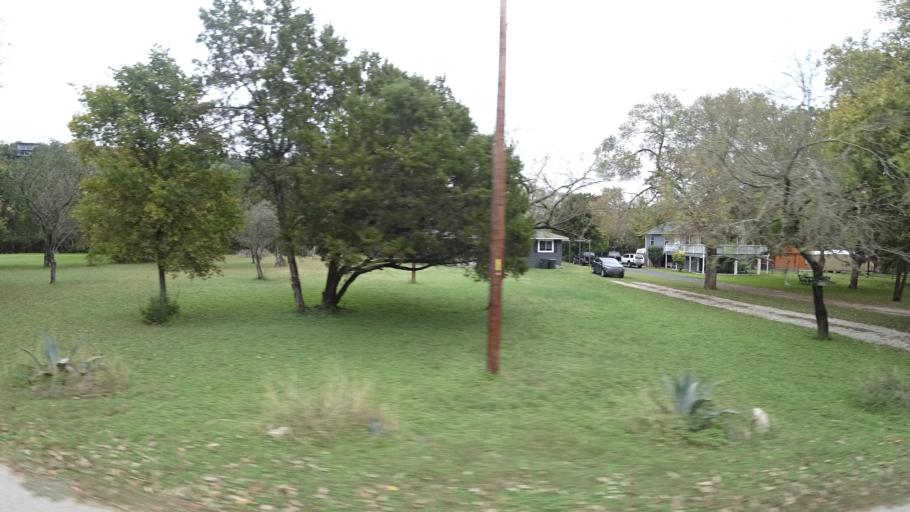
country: US
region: Texas
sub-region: Travis County
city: Hudson Bend
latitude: 30.3784
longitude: -97.9199
